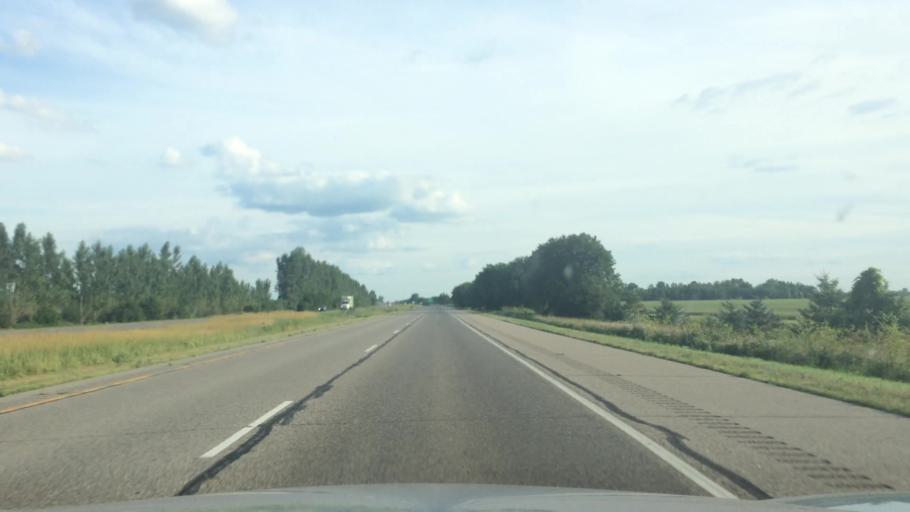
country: US
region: Wisconsin
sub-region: Portage County
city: Plover
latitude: 44.3357
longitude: -89.5231
